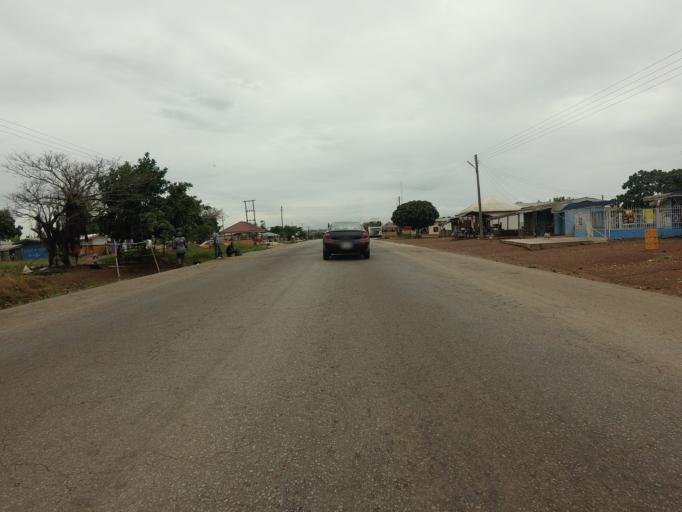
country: GH
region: Eastern
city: Begoro
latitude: 6.3689
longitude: -0.5282
